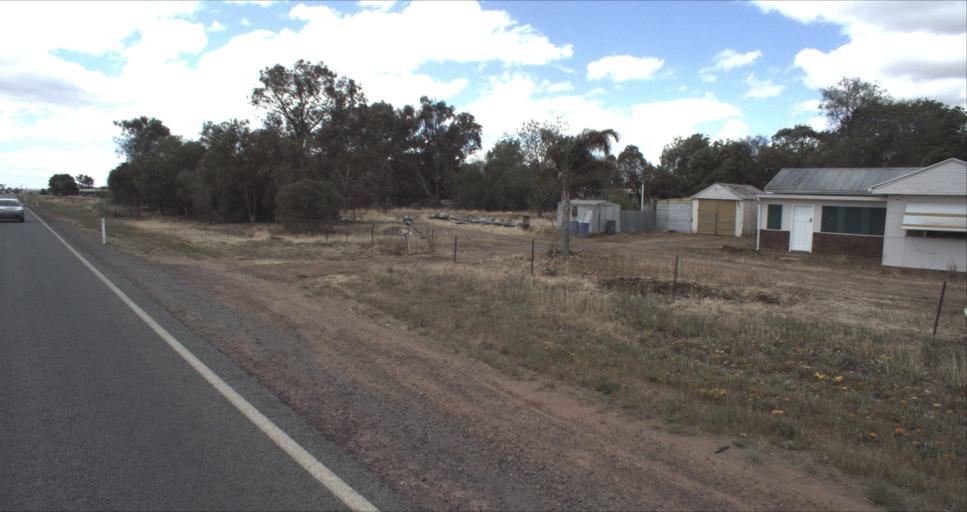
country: AU
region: New South Wales
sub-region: Leeton
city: Leeton
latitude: -34.5937
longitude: 146.4051
